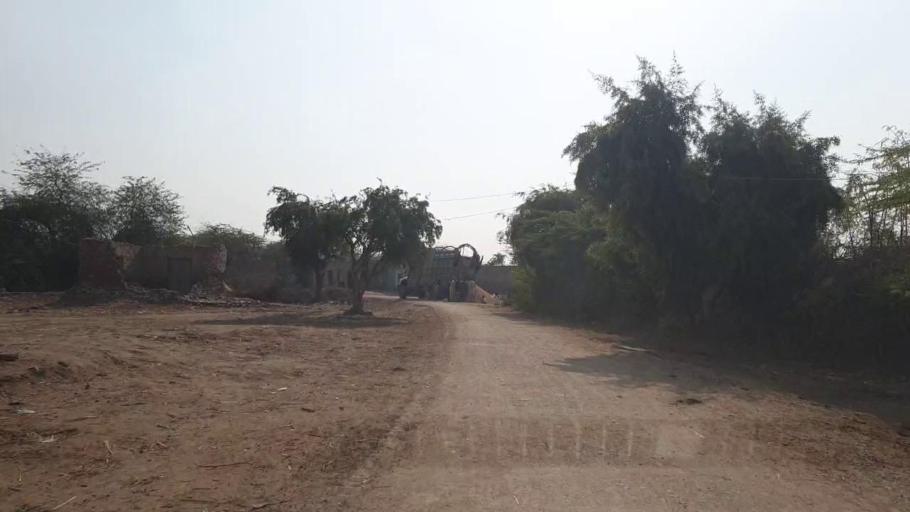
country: PK
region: Sindh
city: Mirwah Gorchani
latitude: 25.3515
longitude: 68.9524
